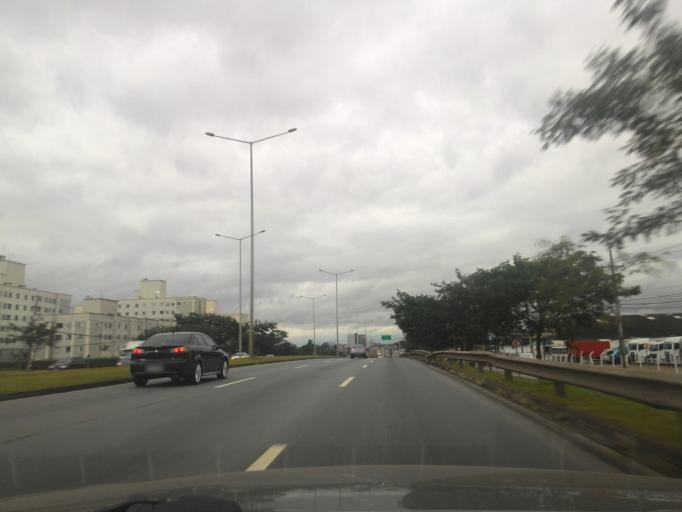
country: BR
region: Parana
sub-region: Sao Jose Dos Pinhais
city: Sao Jose dos Pinhais
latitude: -25.5115
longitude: -49.2880
